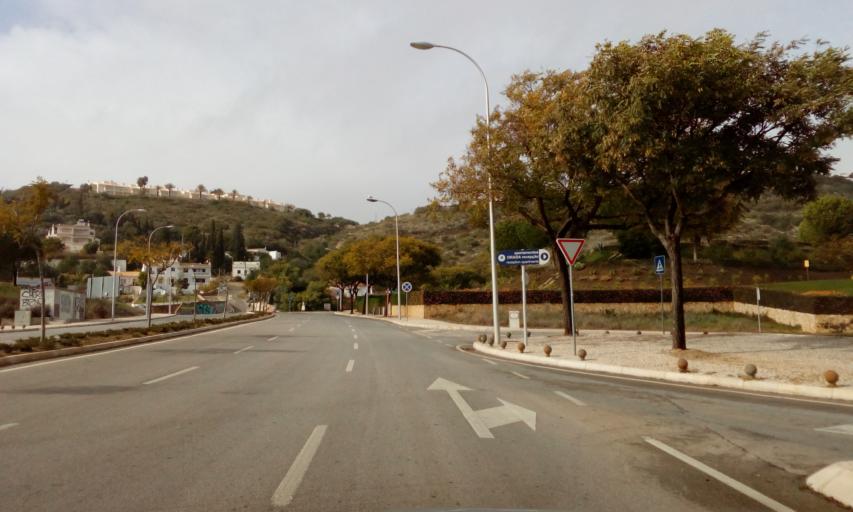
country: PT
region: Faro
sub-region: Albufeira
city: Albufeira
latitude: 37.0866
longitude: -8.2698
